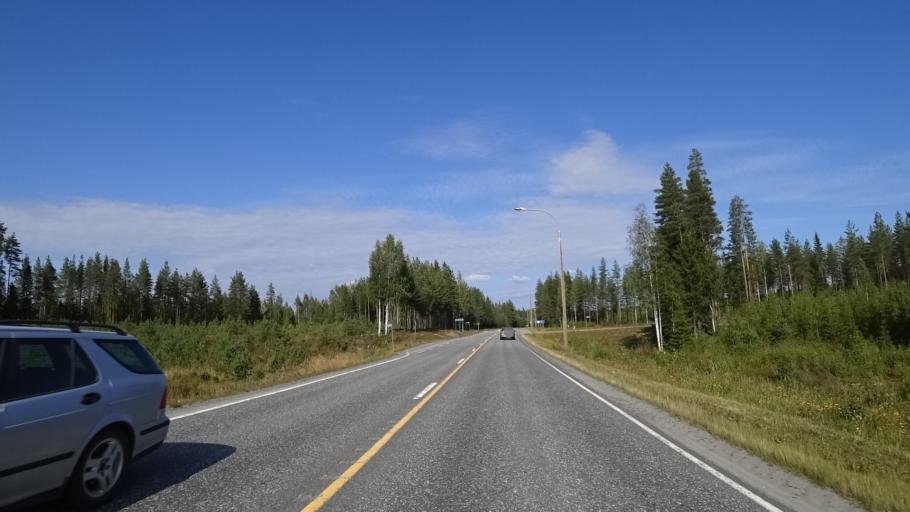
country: FI
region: North Karelia
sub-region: Joensuu
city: Eno
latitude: 62.7709
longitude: 30.0483
